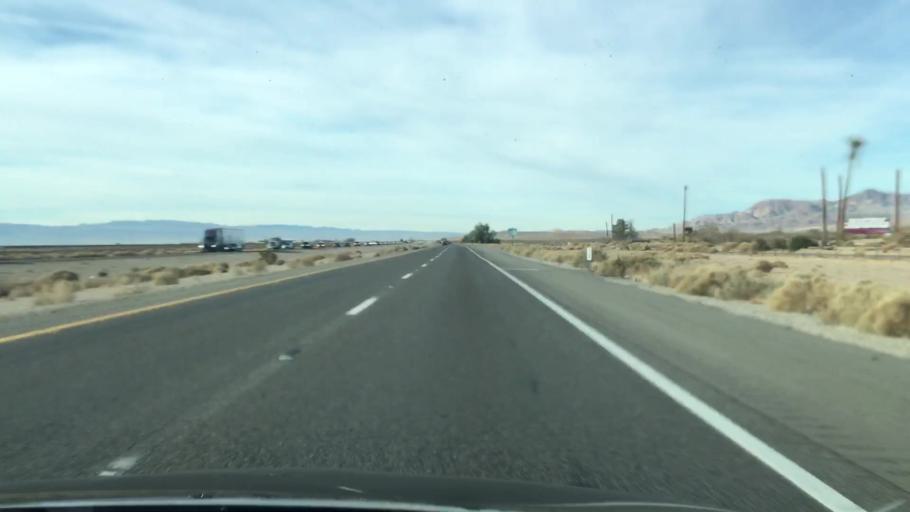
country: US
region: California
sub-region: San Bernardino County
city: Fort Irwin
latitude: 34.9480
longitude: -116.6812
